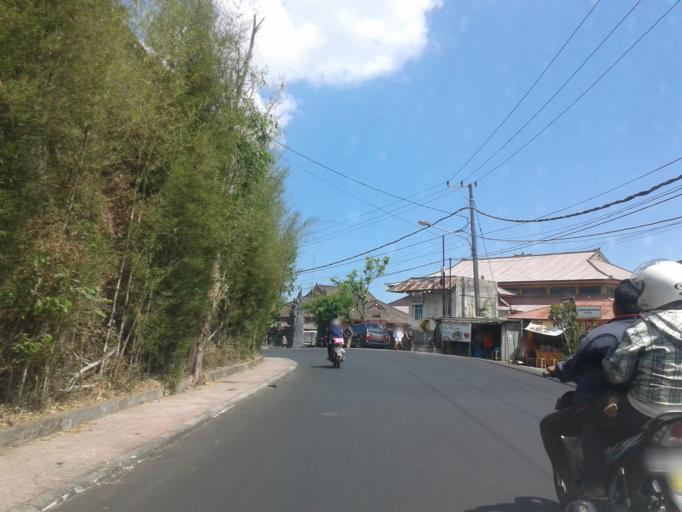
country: ID
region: Bali
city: Banjar Kedisan
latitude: -8.2809
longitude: 115.3606
